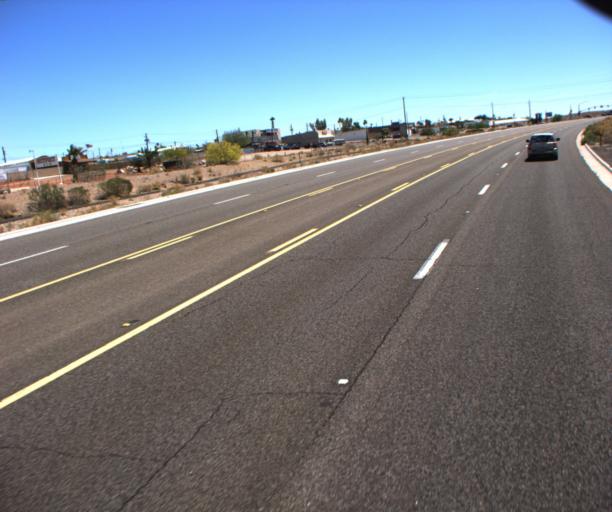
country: US
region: Arizona
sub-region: Mohave County
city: Lake Havasu City
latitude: 34.4556
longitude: -114.2694
